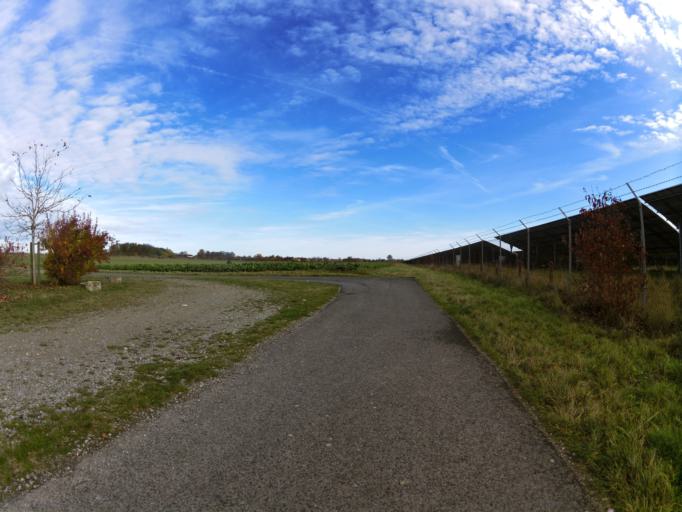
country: DE
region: Bavaria
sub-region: Regierungsbezirk Unterfranken
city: Giebelstadt
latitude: 49.6502
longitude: 9.9606
